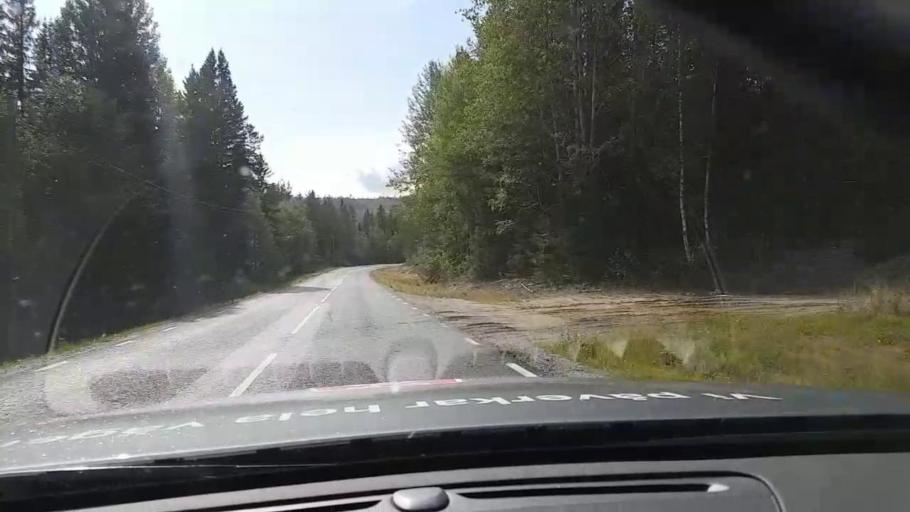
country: SE
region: Vaesterbotten
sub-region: Asele Kommun
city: Asele
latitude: 63.7901
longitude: 17.6015
